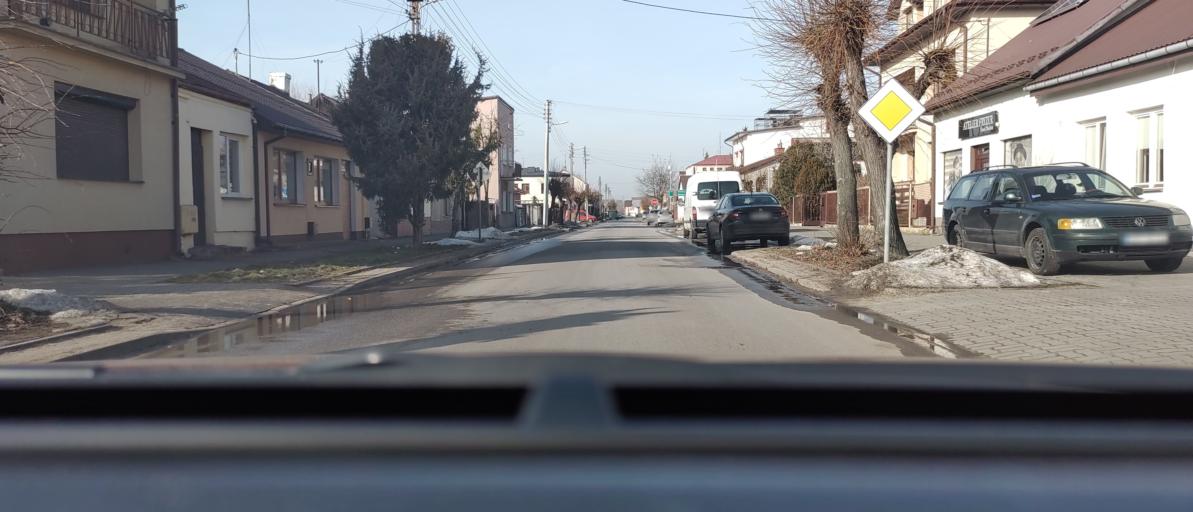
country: PL
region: Masovian Voivodeship
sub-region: Powiat bialobrzeski
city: Bialobrzegi
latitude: 51.6487
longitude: 20.9522
